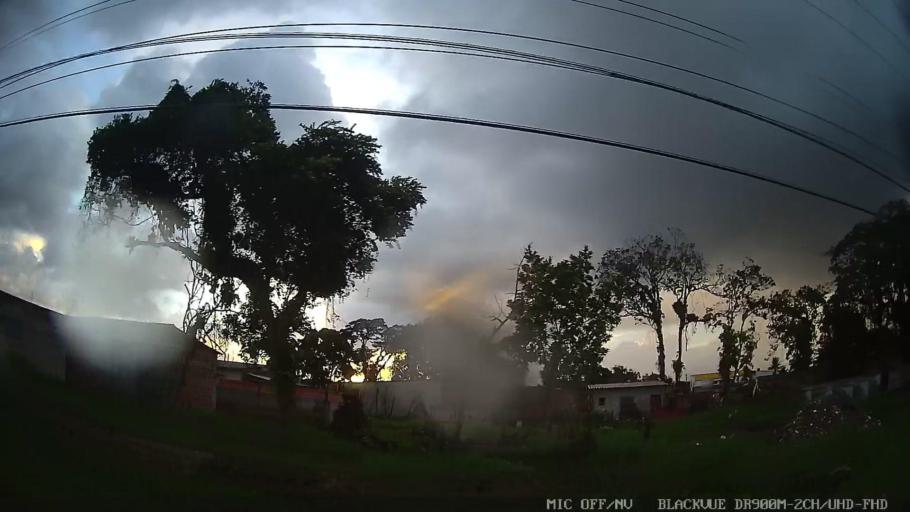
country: BR
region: Sao Paulo
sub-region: Itanhaem
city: Itanhaem
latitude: -24.1563
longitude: -46.7808
